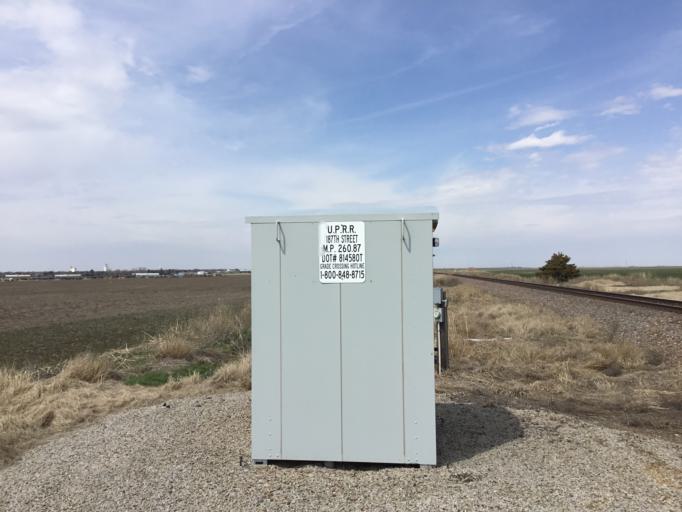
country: US
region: Kansas
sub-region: Russell County
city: Russell
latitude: 38.8865
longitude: -98.8173
